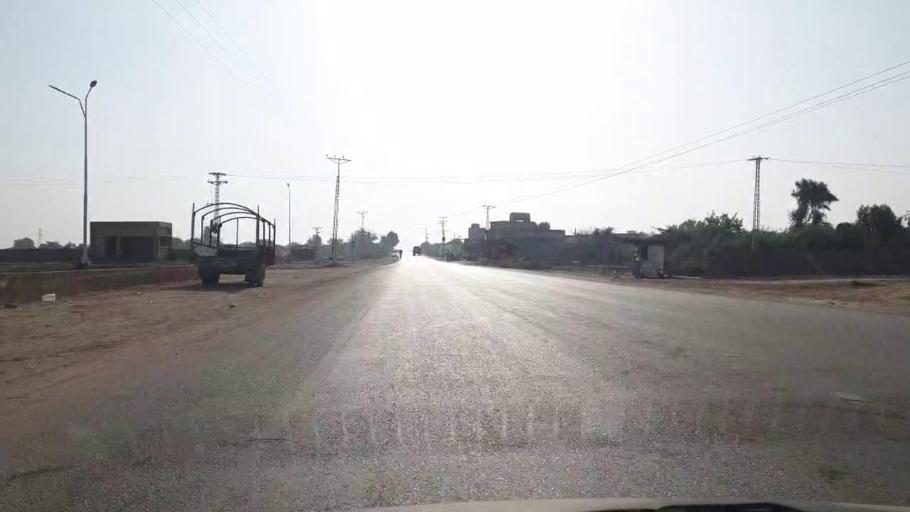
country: PK
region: Sindh
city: Badin
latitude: 24.6767
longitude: 68.8480
